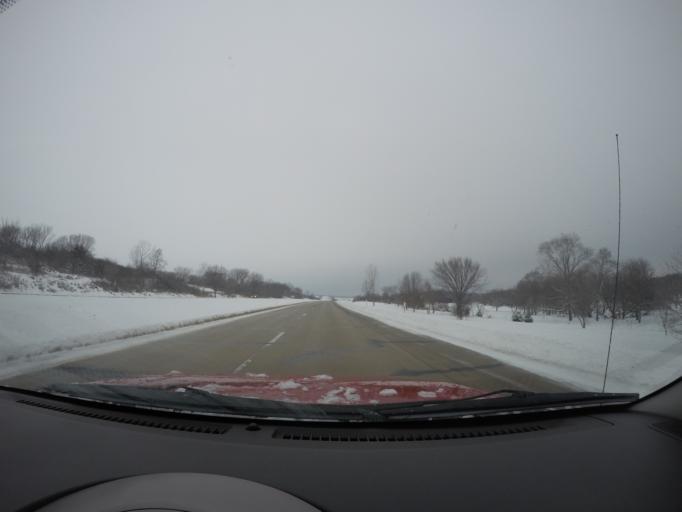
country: US
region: Minnesota
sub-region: Olmsted County
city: Rochester
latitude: 43.9611
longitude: -92.3847
